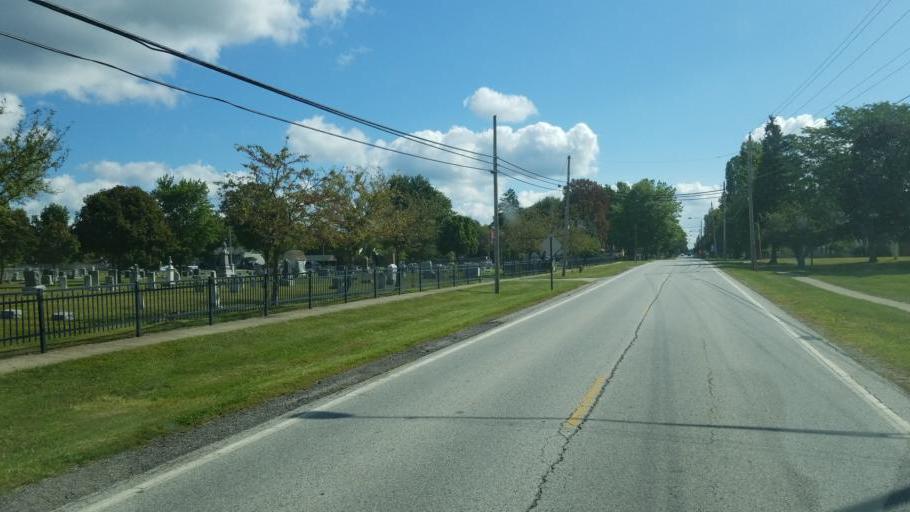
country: US
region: Ohio
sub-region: Lorain County
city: Lagrange
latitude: 41.2373
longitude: -82.1269
